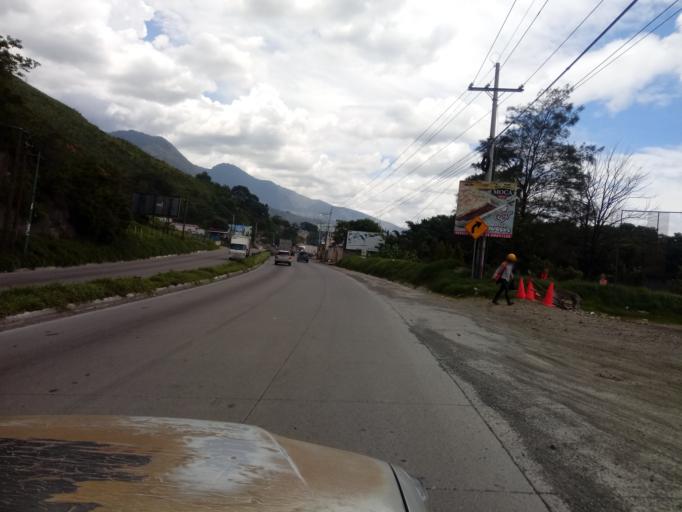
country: GT
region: Escuintla
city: San Vicente Pacaya
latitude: 14.4553
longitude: -90.6431
